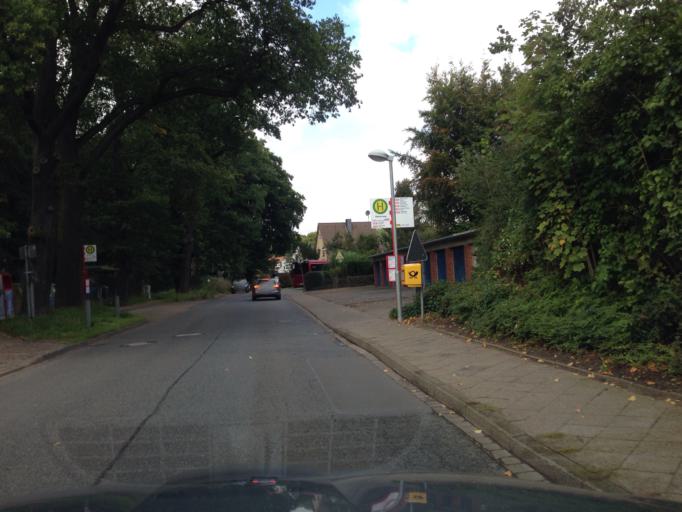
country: DE
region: Lower Saxony
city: Lueneburg
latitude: 53.2597
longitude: 10.4321
